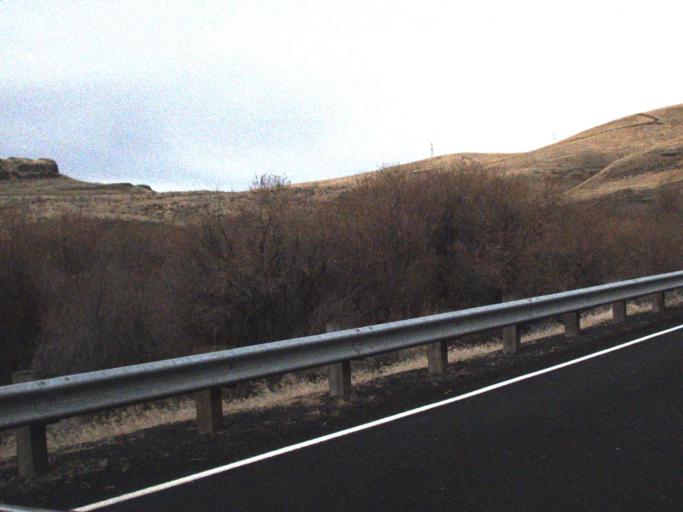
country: US
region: Washington
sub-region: Walla Walla County
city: Waitsburg
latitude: 46.5545
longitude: -118.1784
